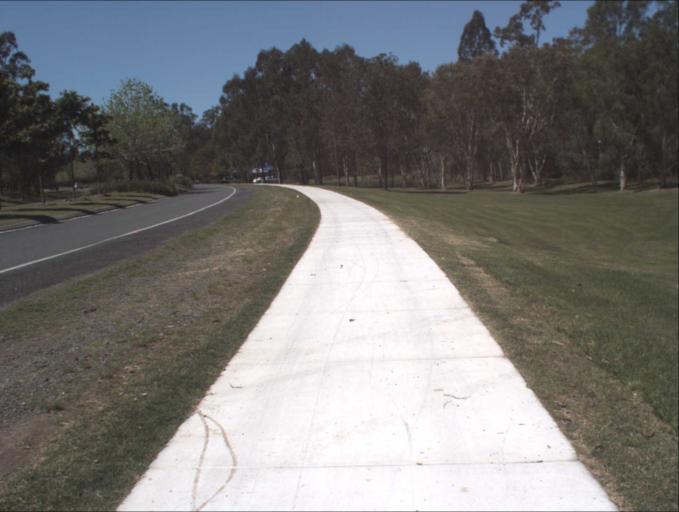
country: AU
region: Queensland
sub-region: Logan
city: North Maclean
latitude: -27.8136
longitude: 152.9620
